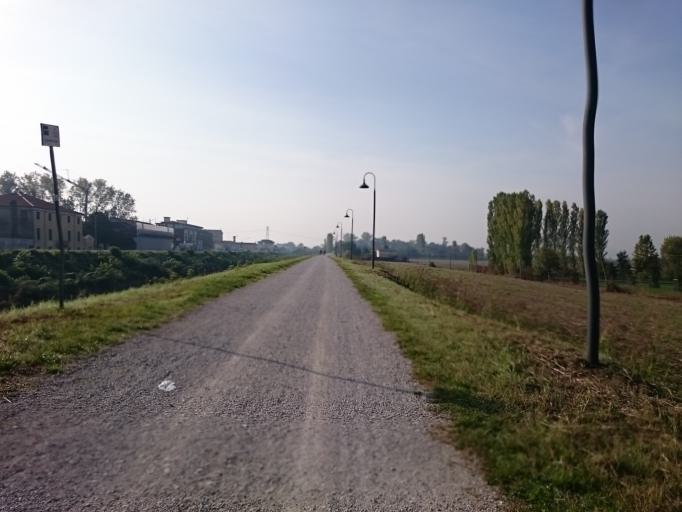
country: IT
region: Veneto
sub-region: Provincia di Padova
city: Mandriola-Sant'Agostino
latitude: 45.3677
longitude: 11.8431
